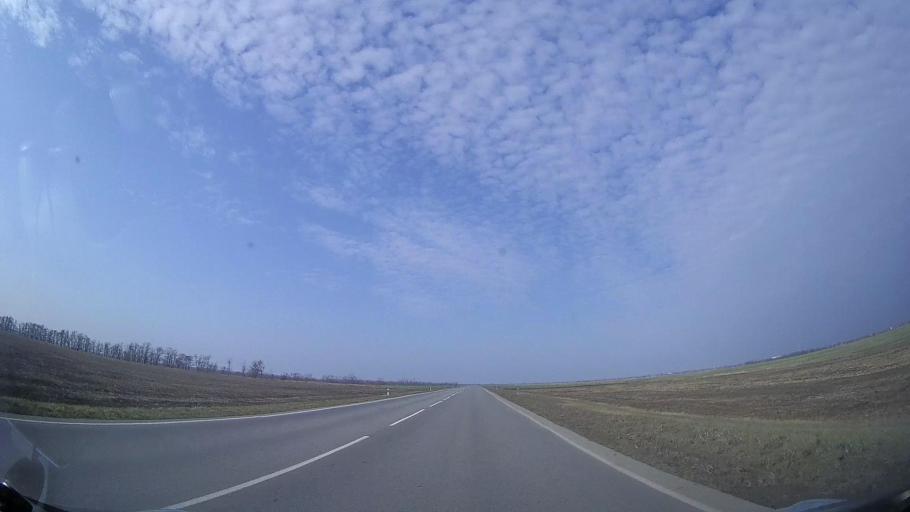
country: RU
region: Rostov
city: Tselina
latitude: 46.5126
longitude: 41.0615
